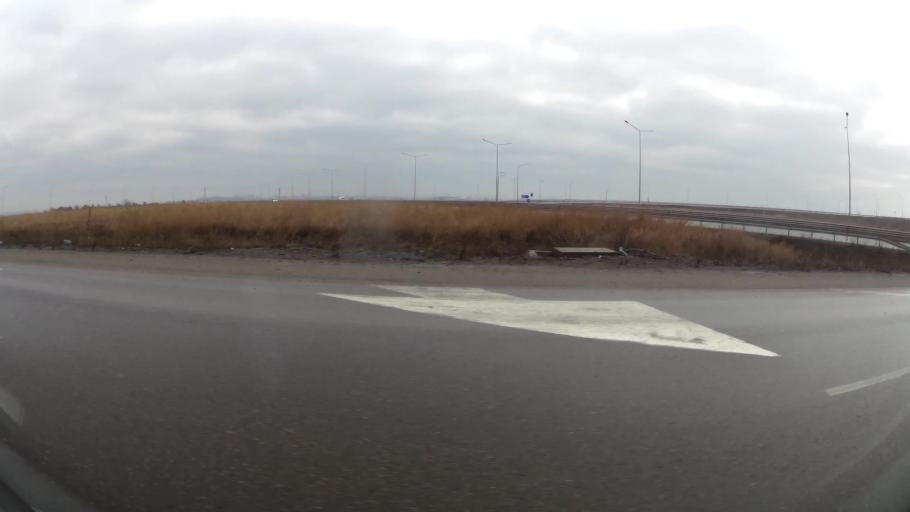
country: BG
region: Sofia-Capital
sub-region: Stolichna Obshtina
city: Sofia
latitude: 42.7700
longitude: 23.2881
